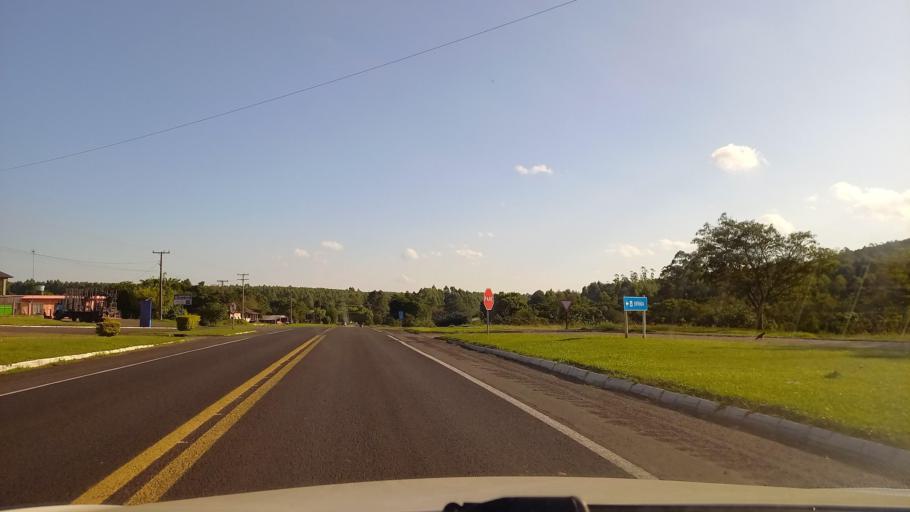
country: BR
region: Rio Grande do Sul
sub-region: Taquari
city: Taquari
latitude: -29.7095
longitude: -51.7657
